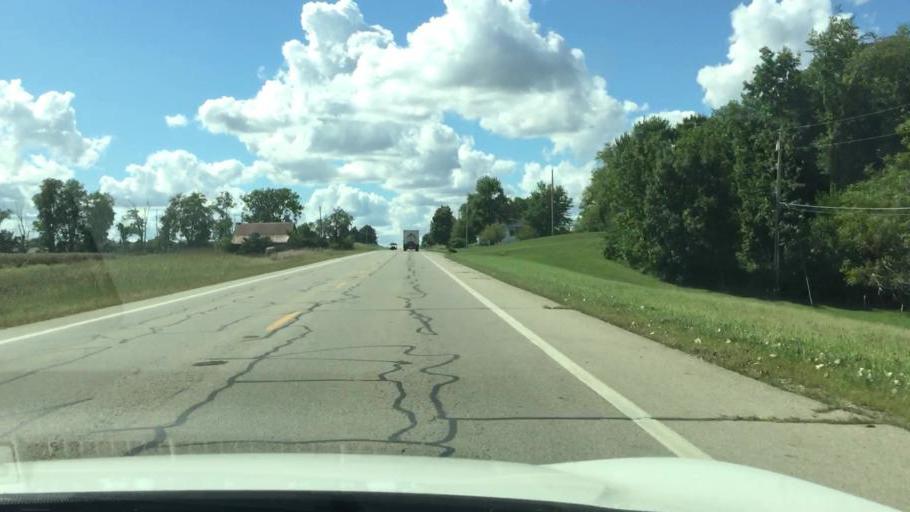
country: US
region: Ohio
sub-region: Champaign County
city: Mechanicsburg
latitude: 40.0777
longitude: -83.6049
